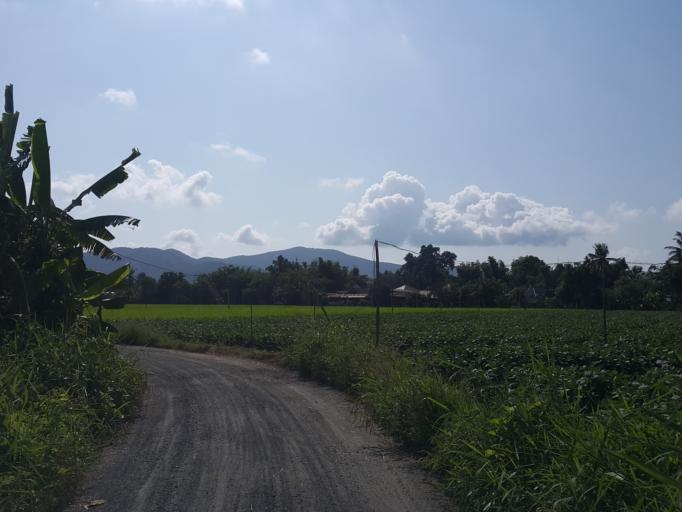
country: TH
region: Chiang Mai
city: San Kamphaeng
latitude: 18.8237
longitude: 99.1655
